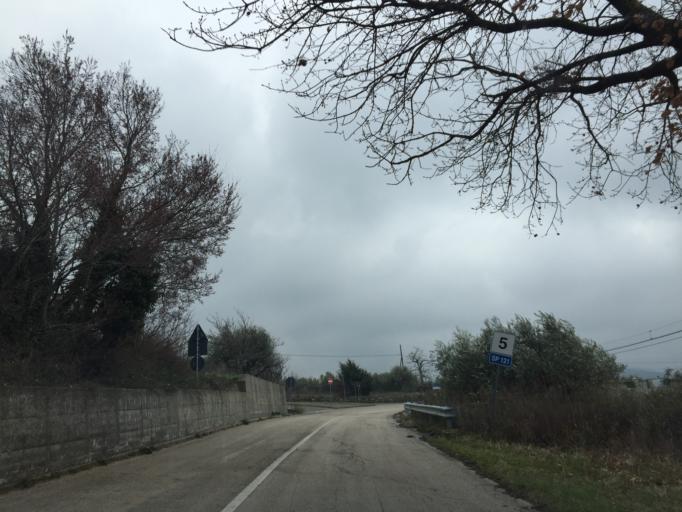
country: IT
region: Apulia
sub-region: Provincia di Foggia
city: Bovino
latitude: 41.2586
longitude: 15.3530
